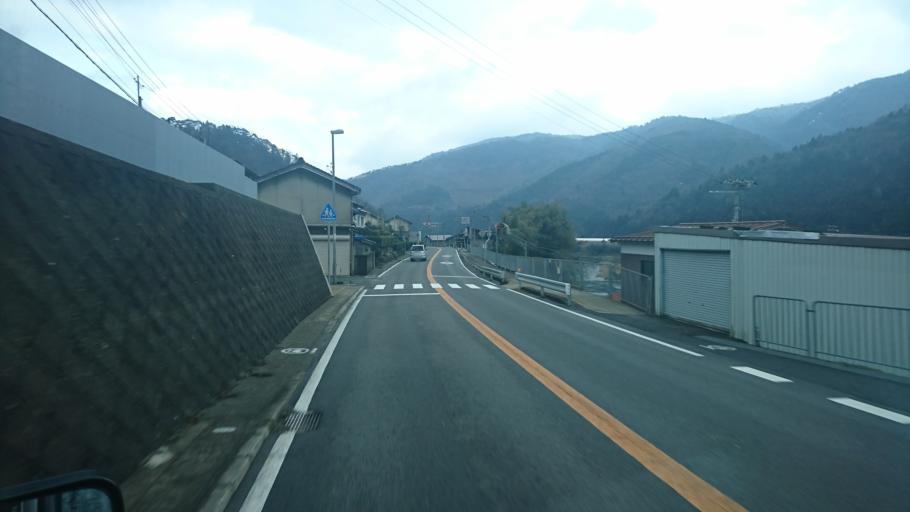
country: JP
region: Hyogo
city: Toyooka
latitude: 35.3813
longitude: 134.6589
